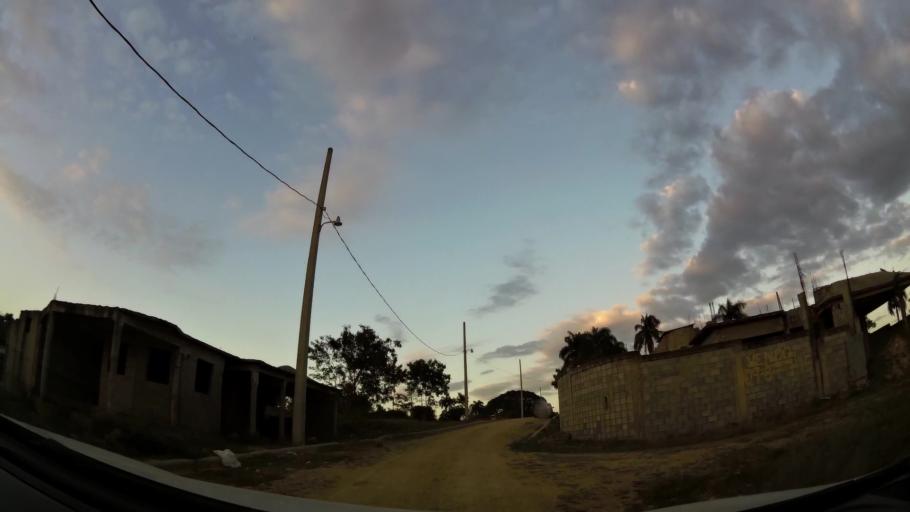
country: DO
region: Nacional
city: La Agustina
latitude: 18.5689
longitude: -69.9393
